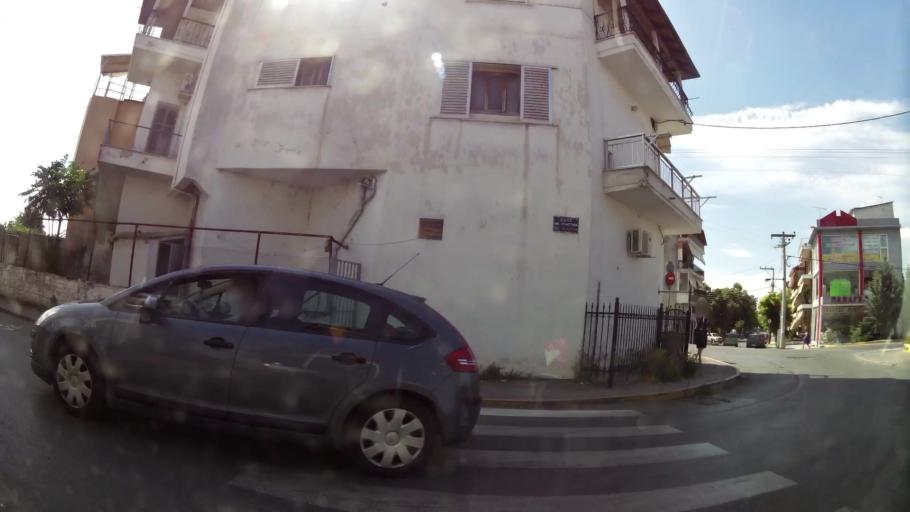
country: GR
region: Central Macedonia
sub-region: Nomos Pierias
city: Katerini
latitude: 40.2727
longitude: 22.4910
